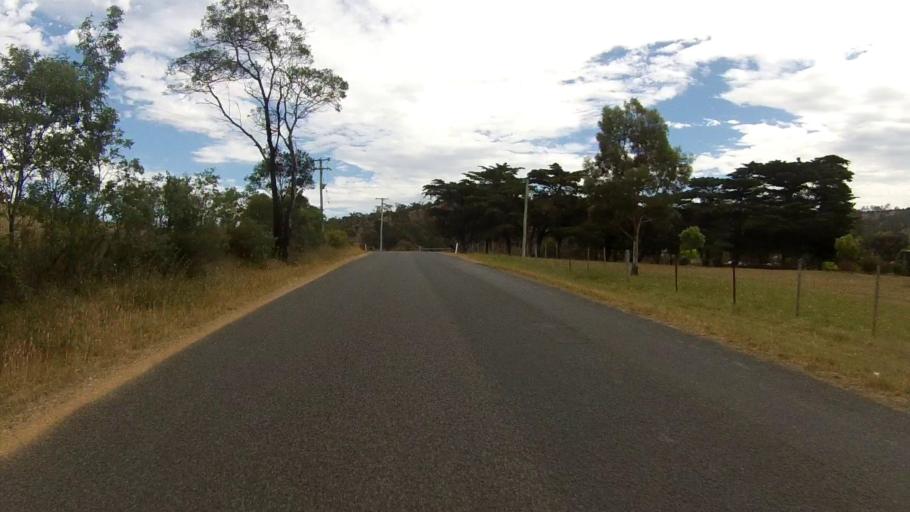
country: AU
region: Tasmania
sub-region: Clarence
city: Lindisfarne
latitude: -42.7438
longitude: 147.3685
